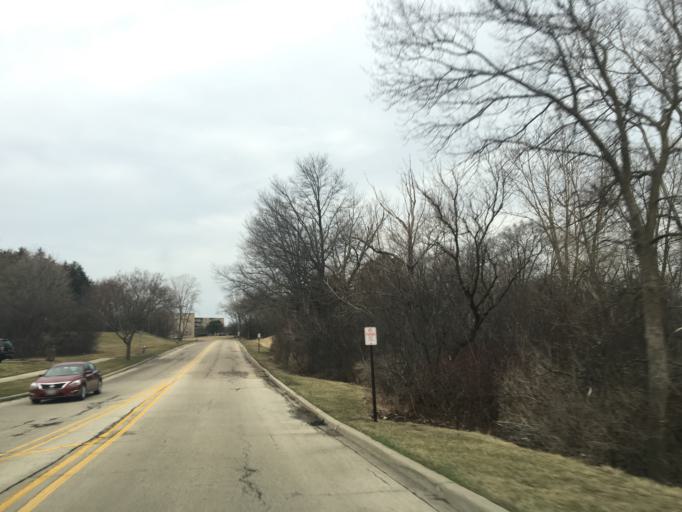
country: US
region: Illinois
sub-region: Cook County
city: Hoffman Estates
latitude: 42.0556
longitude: -88.0814
